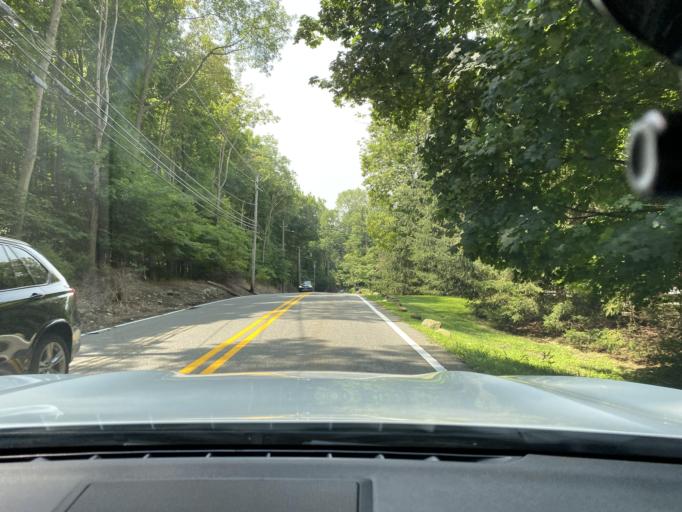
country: US
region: New Jersey
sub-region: Bergen County
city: Franklin Lakes
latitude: 41.0542
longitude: -74.2149
